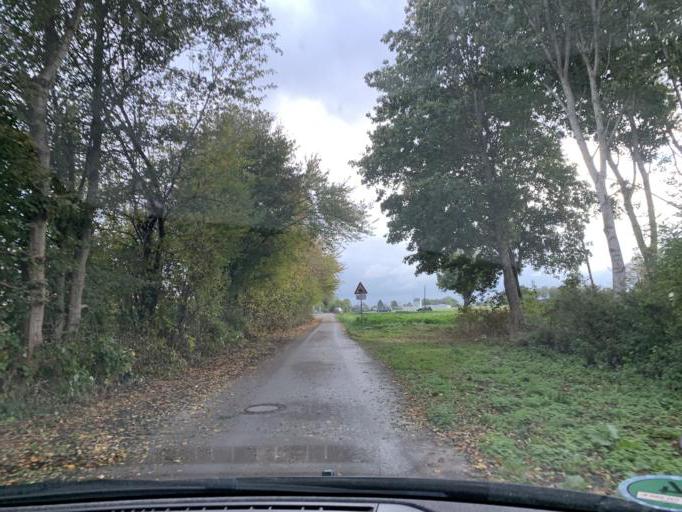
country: DE
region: North Rhine-Westphalia
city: Erkelenz
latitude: 51.1006
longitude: 6.3614
